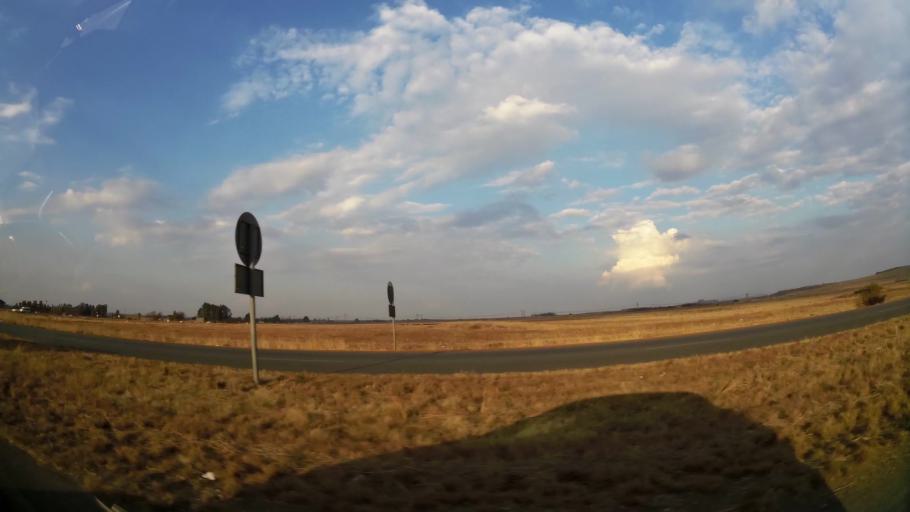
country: ZA
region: Gauteng
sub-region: Sedibeng District Municipality
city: Vanderbijlpark
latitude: -26.6208
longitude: 27.8121
